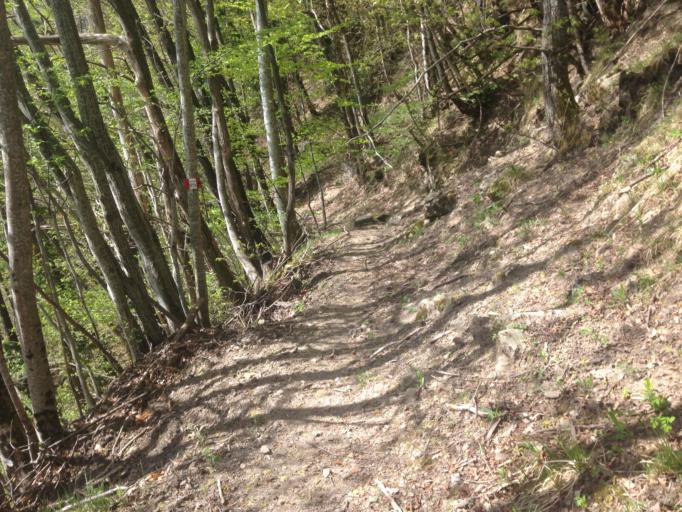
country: IT
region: Emilia-Romagna
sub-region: Provincia di Bologna
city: Lizzano in Belvedere
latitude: 44.1586
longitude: 10.8886
